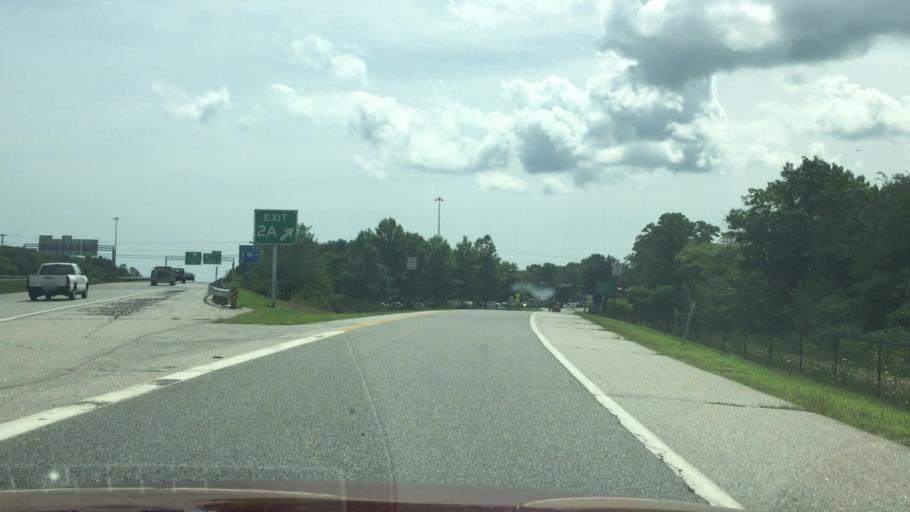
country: US
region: Maine
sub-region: York County
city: Saco
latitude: 43.5127
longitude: -70.4351
